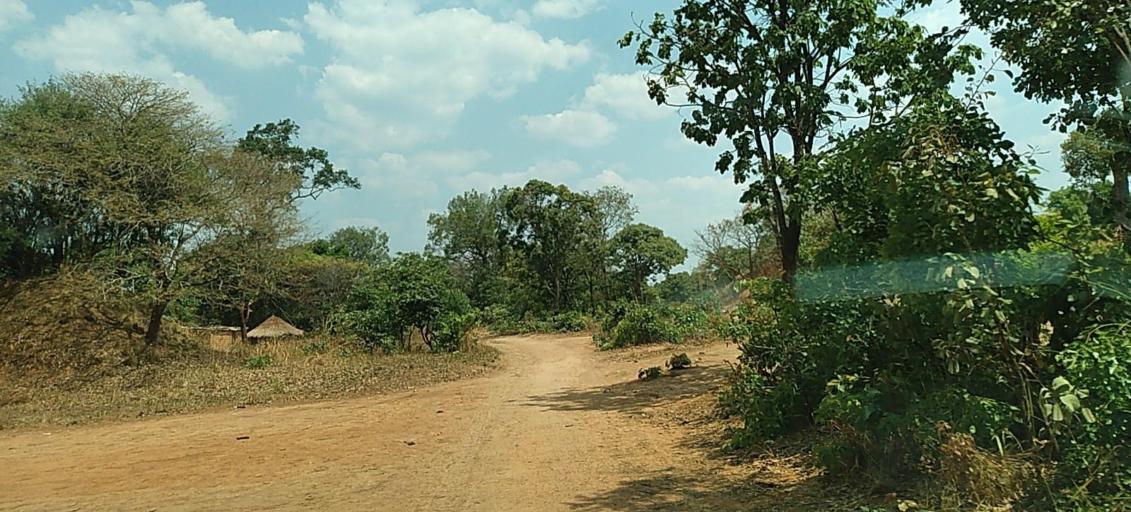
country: CD
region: Katanga
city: Kipushi
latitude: -12.0370
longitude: 27.4365
